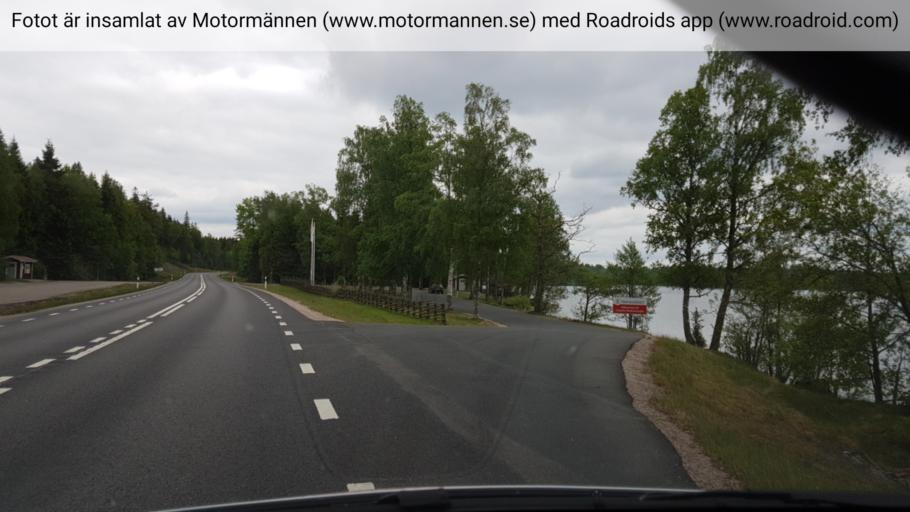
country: SE
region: Kronoberg
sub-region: Vaxjo Kommun
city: Braas
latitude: 57.2374
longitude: 15.1443
